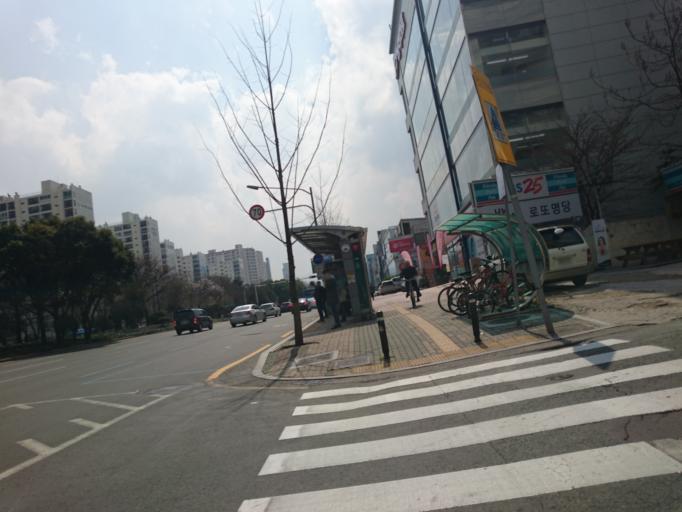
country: KR
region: Daegu
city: Daegu
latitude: 35.8574
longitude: 128.6255
